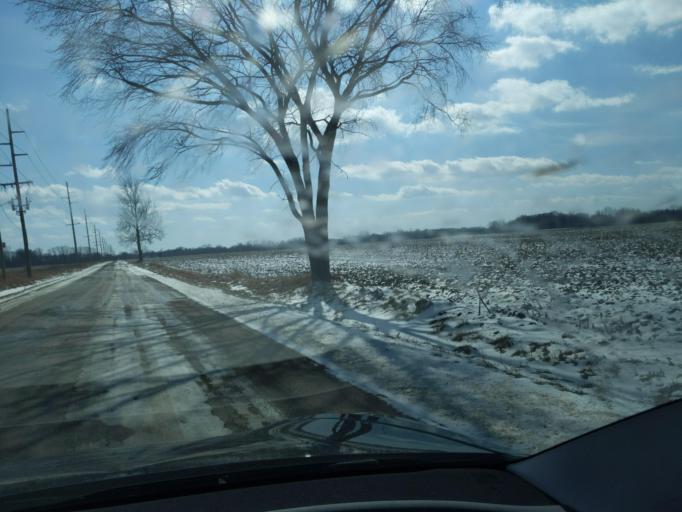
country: US
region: Michigan
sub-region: Livingston County
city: Fowlerville
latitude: 42.6424
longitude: -84.0920
